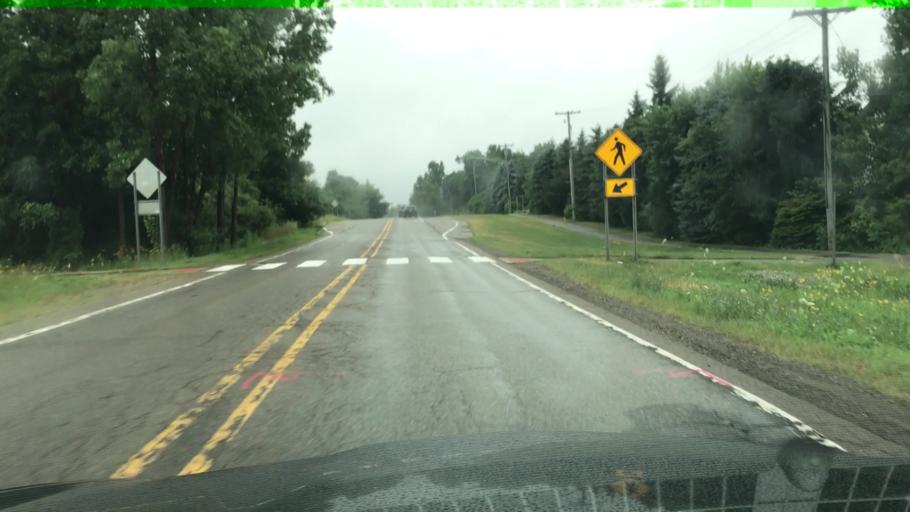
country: US
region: Michigan
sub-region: Oakland County
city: Lake Orion
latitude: 42.7331
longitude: -83.2881
